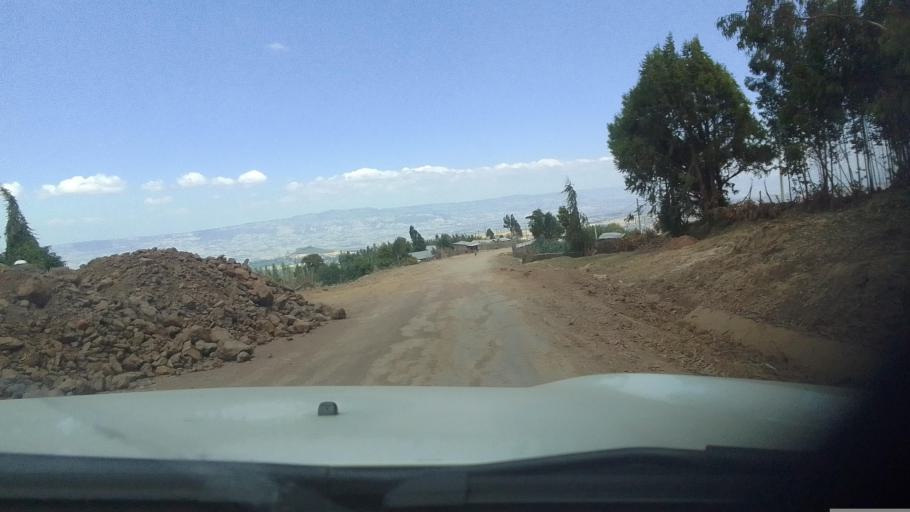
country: ET
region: Oromiya
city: Hagere Hiywet
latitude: 8.8435
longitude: 37.8854
